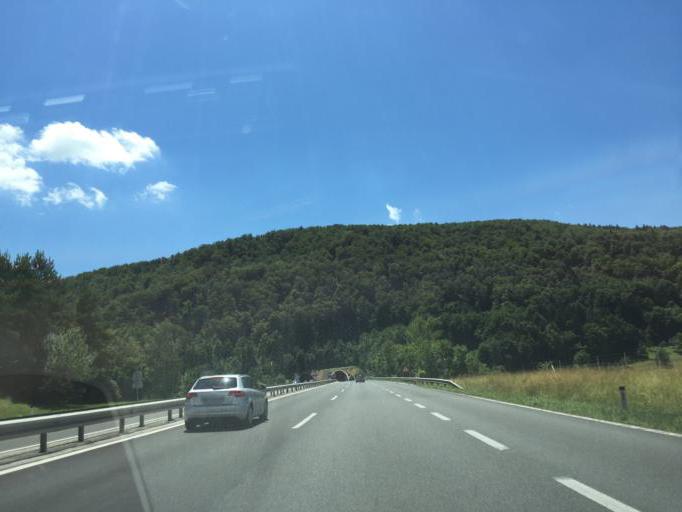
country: SI
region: Slovenska Konjice
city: Slovenske Konjice
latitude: 46.3207
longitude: 15.4612
